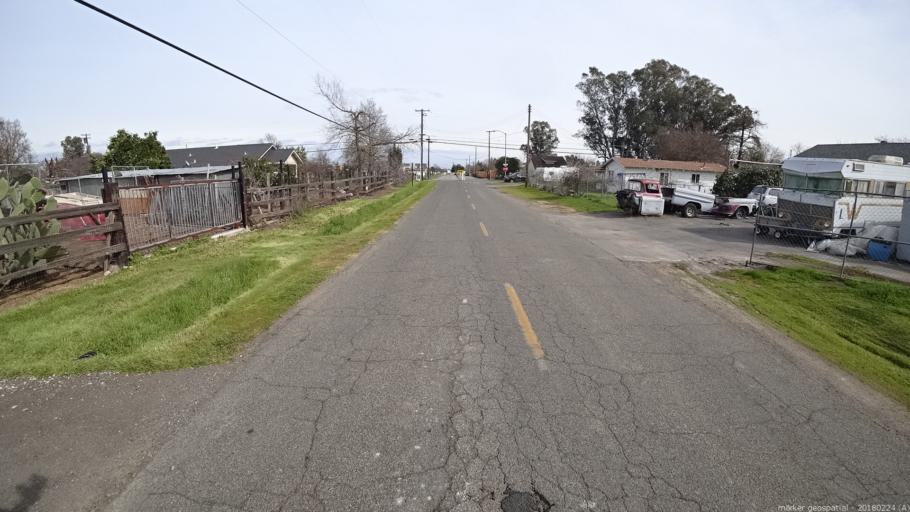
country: US
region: California
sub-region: Sacramento County
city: Elverta
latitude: 38.7100
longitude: -121.4519
